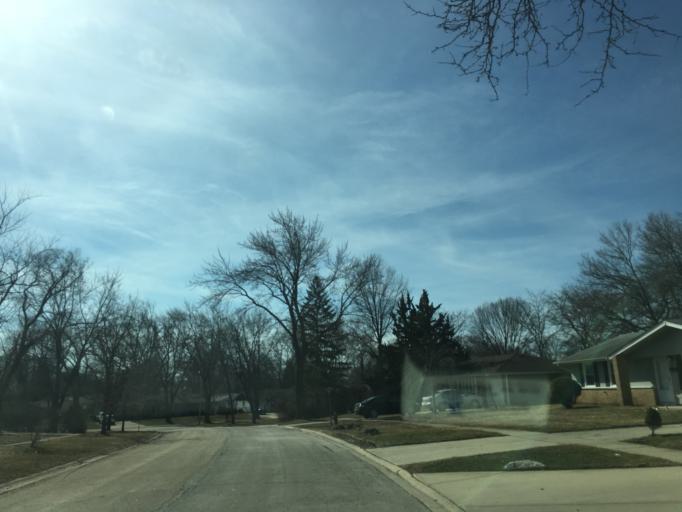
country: US
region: Illinois
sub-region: DuPage County
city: Hanover Park
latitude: 42.0211
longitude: -88.1226
